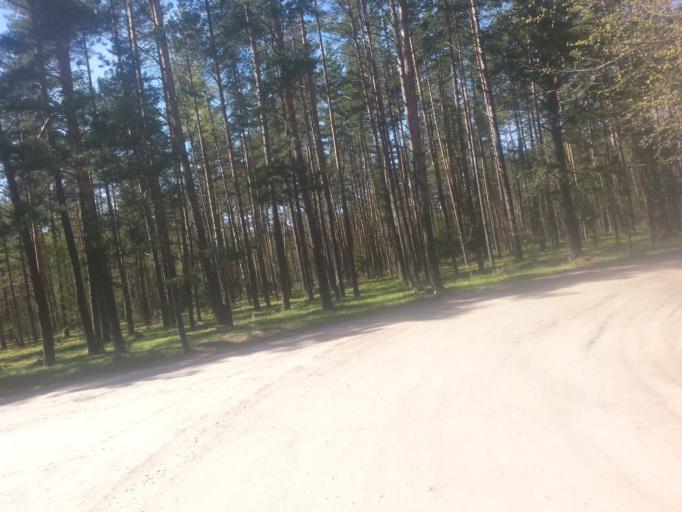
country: BY
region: Minsk
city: Narach
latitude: 54.9256
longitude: 26.6785
